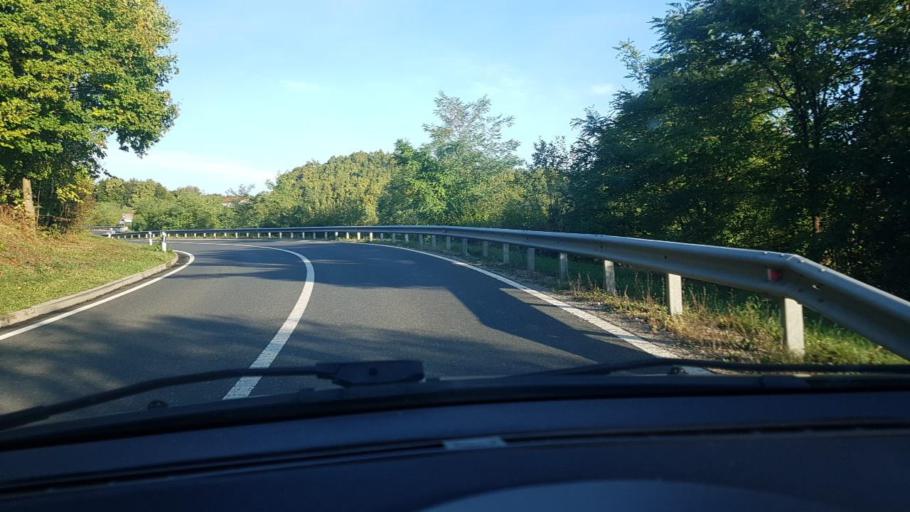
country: HR
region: Krapinsko-Zagorska
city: Marija Bistrica
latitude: 45.9565
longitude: 16.0932
